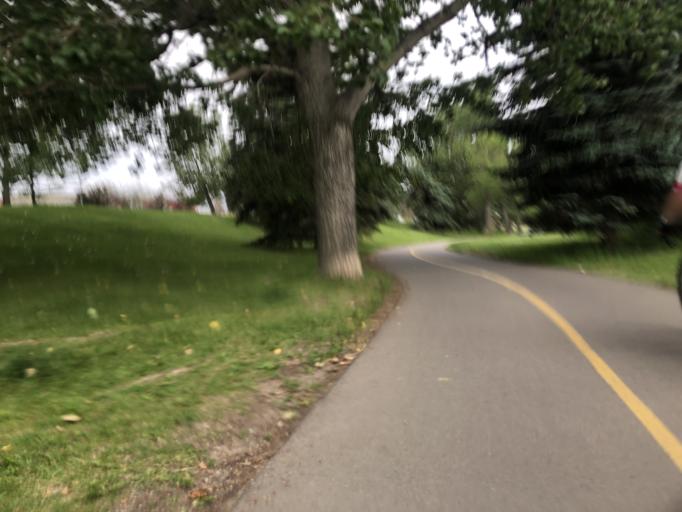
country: CA
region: Alberta
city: Calgary
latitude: 51.0424
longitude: -114.0310
